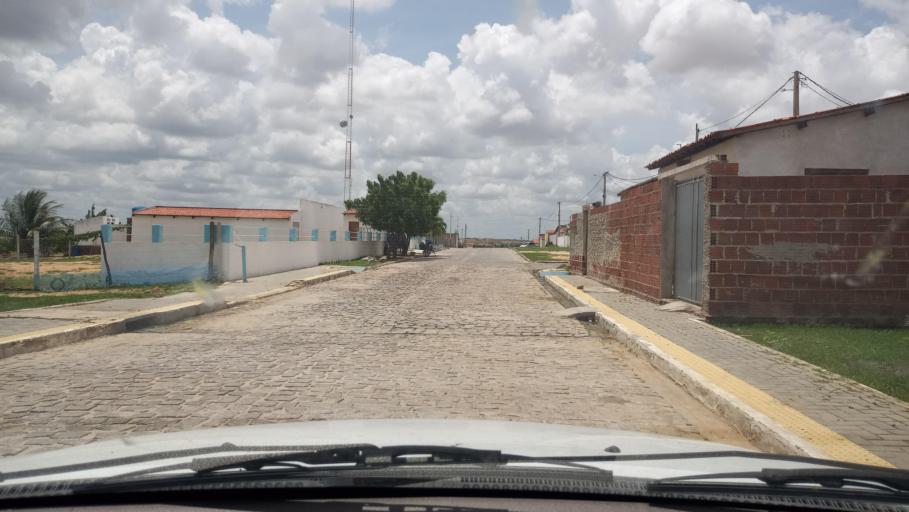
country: BR
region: Rio Grande do Norte
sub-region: Tangara
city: Tangara
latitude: -6.0963
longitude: -35.7084
